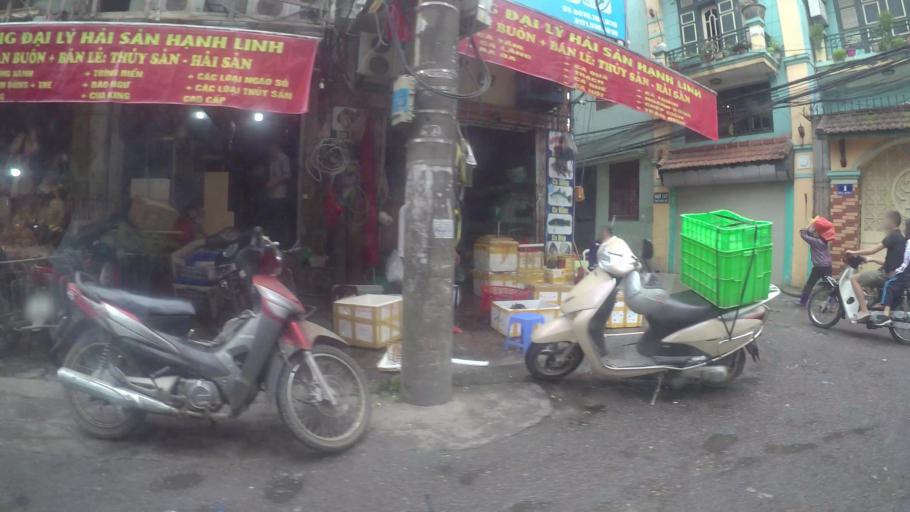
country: VN
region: Ha Noi
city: Hoan Kiem
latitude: 21.0425
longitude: 105.8511
